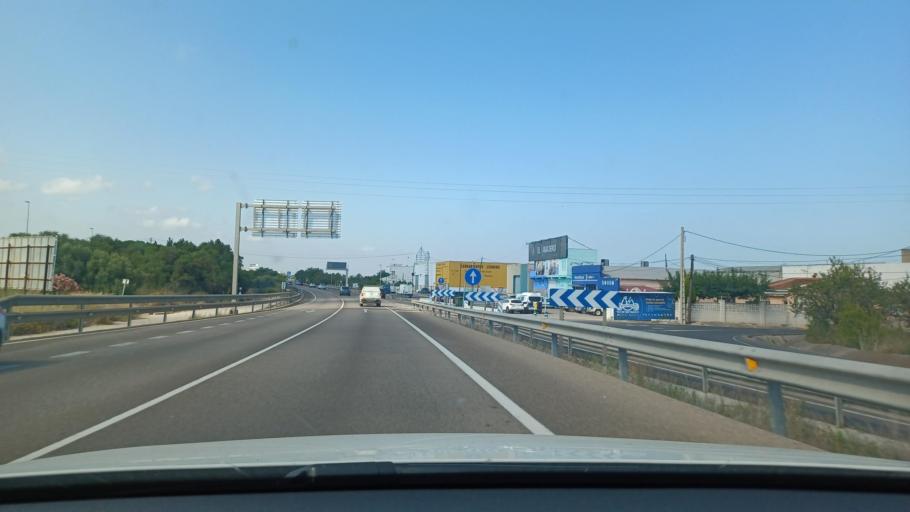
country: ES
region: Valencia
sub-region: Provincia de Castello
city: Orpesa/Oropesa del Mar
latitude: 40.0979
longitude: 0.1338
